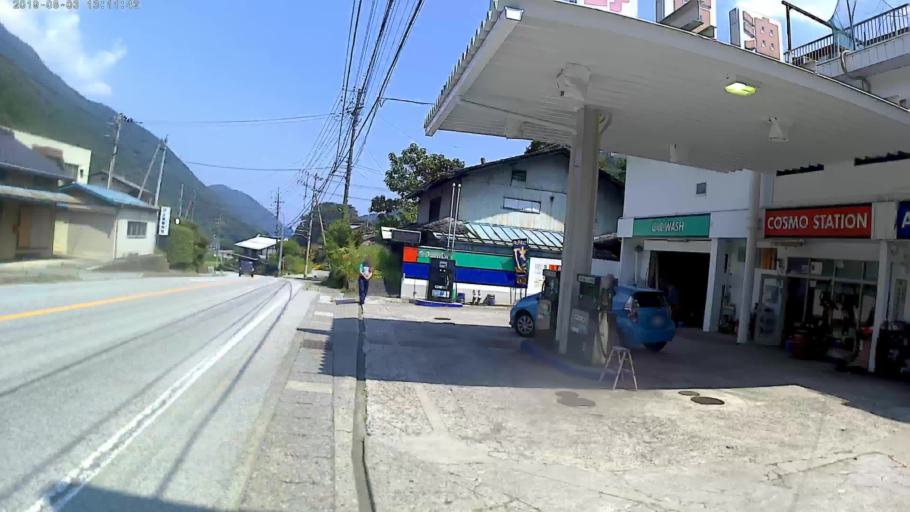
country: JP
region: Yamanashi
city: Enzan
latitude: 35.6050
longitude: 138.8091
